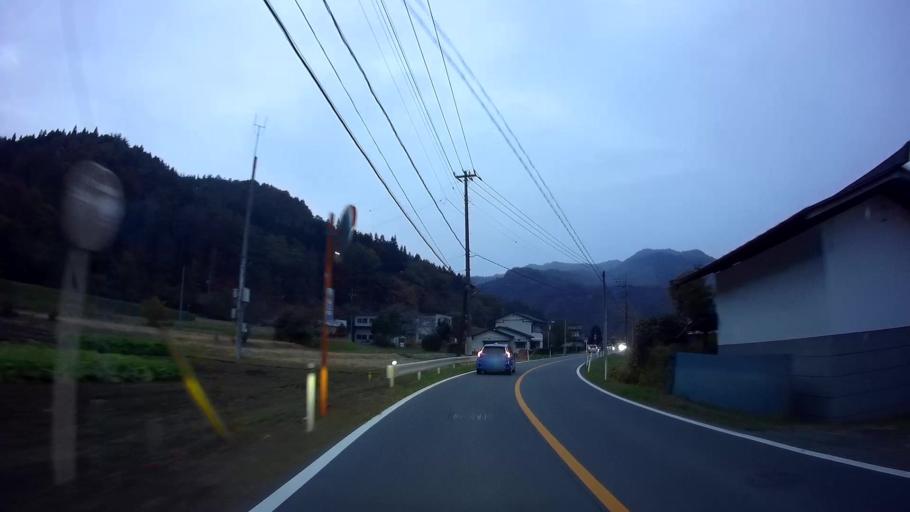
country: JP
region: Gunma
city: Nakanojomachi
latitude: 36.5337
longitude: 138.7841
